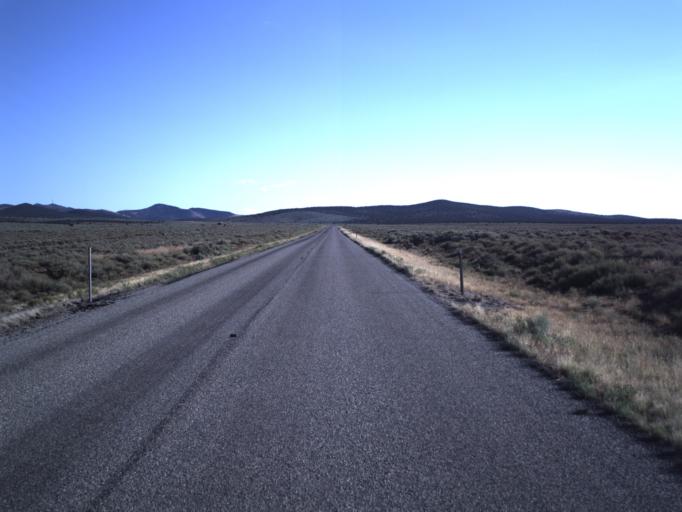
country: US
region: Utah
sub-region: Iron County
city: Enoch
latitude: 37.9942
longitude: -112.9999
